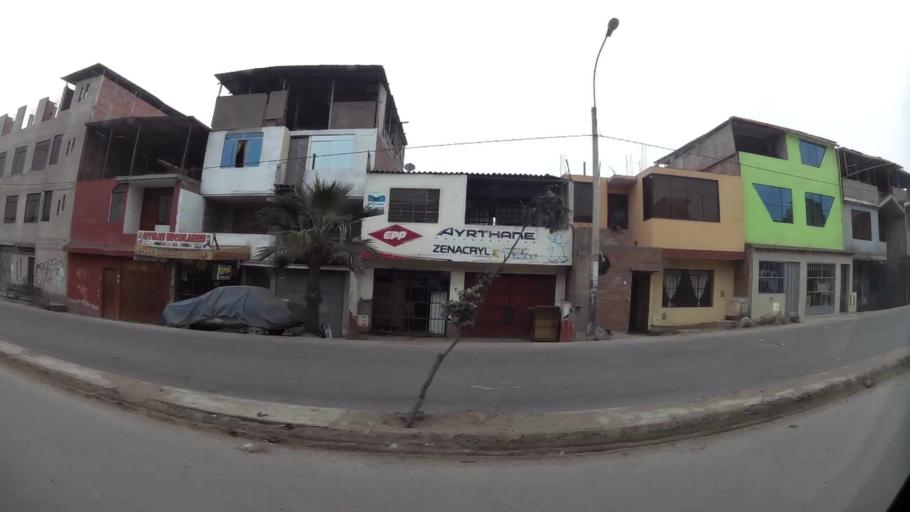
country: PE
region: Lima
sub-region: Lima
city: Surco
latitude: -12.2267
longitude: -76.9287
